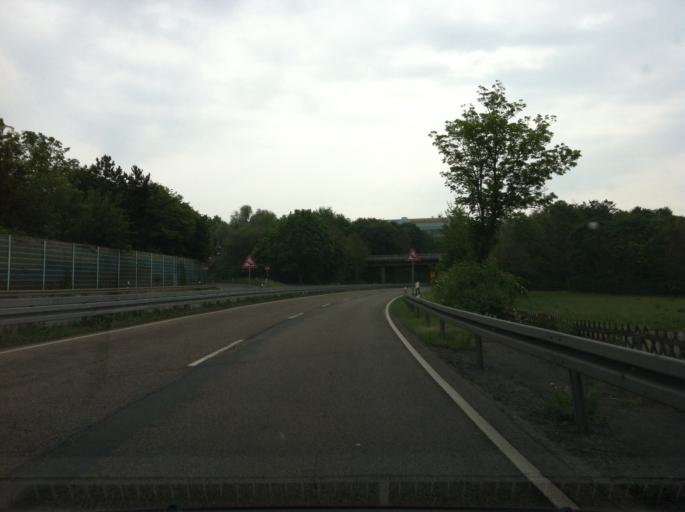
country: DE
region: Hesse
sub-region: Regierungsbezirk Darmstadt
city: Eschborn
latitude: 50.1384
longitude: 8.5758
